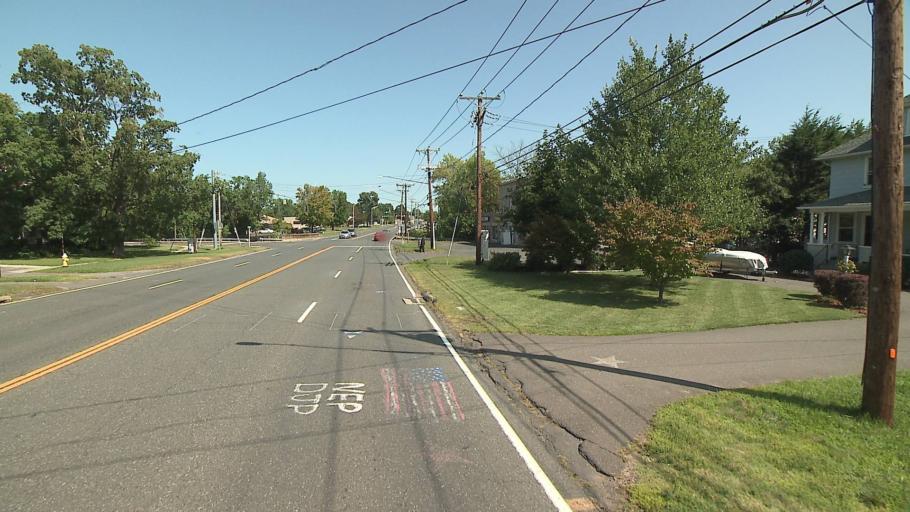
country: US
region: Connecticut
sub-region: Hartford County
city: Thompsonville
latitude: 41.9959
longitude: -72.5944
